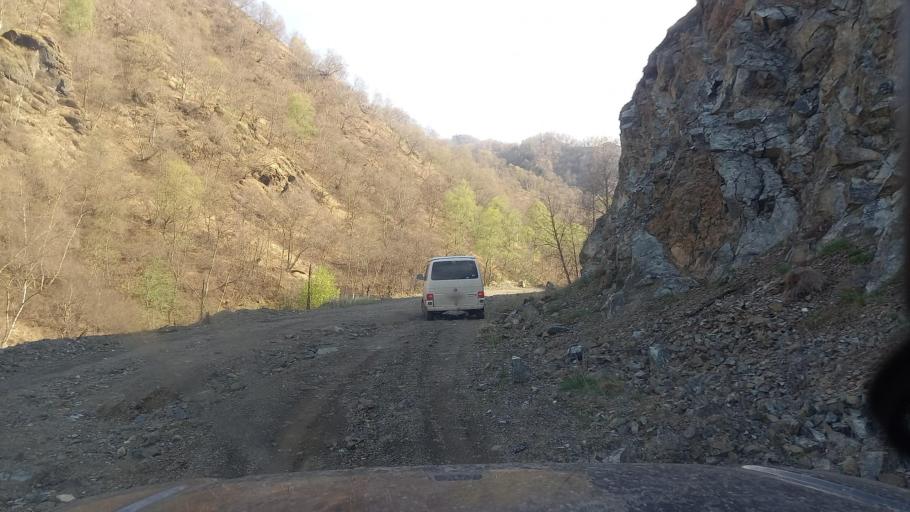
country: RU
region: Kabardino-Balkariya
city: Kamennomostskoye
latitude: 43.7008
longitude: 42.8431
